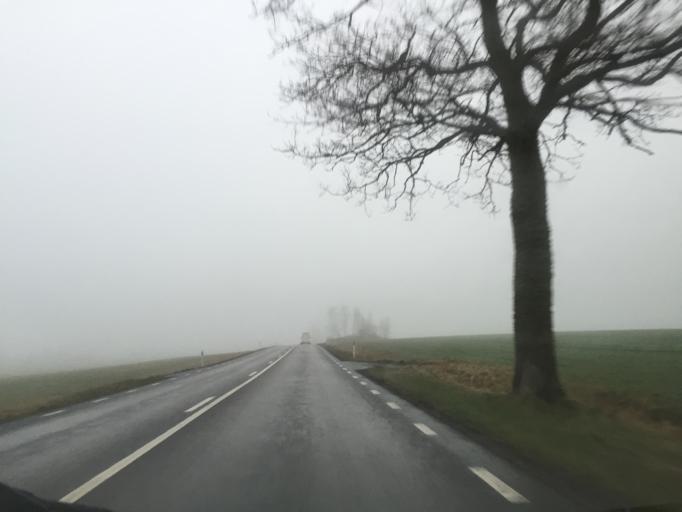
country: SE
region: Soedermanland
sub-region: Katrineholms Kommun
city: Katrineholm
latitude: 58.9394
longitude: 16.3979
